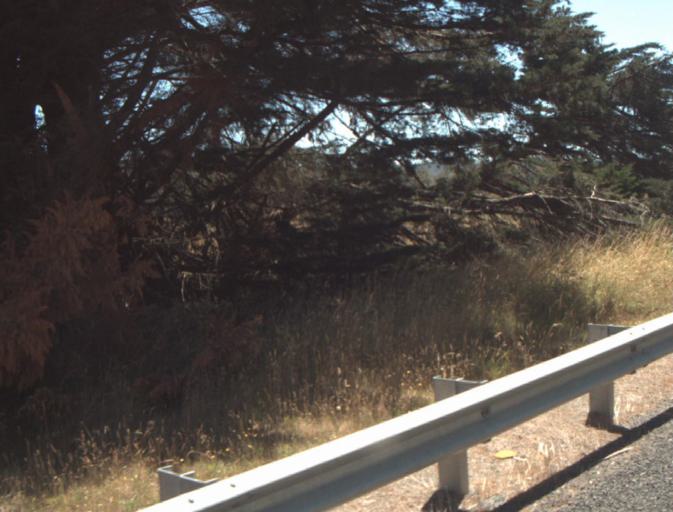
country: AU
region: Tasmania
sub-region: Launceston
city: Newstead
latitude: -41.3694
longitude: 147.3226
